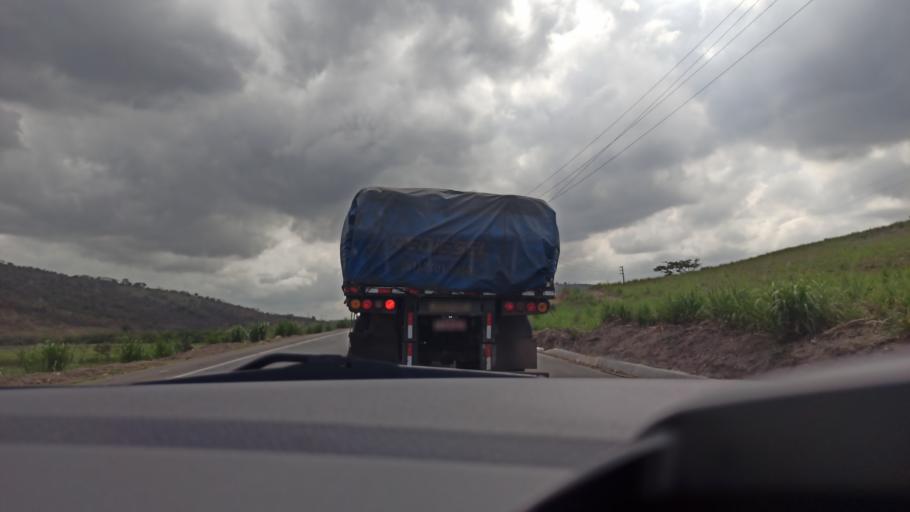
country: BR
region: Pernambuco
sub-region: Timbauba
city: Timbauba
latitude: -7.5226
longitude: -35.2951
